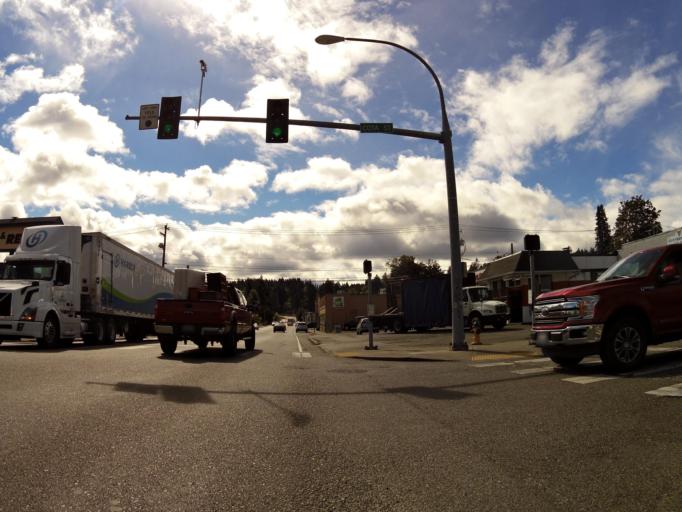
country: US
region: Washington
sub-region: Mason County
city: Shelton
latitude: 47.2121
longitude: -123.1003
